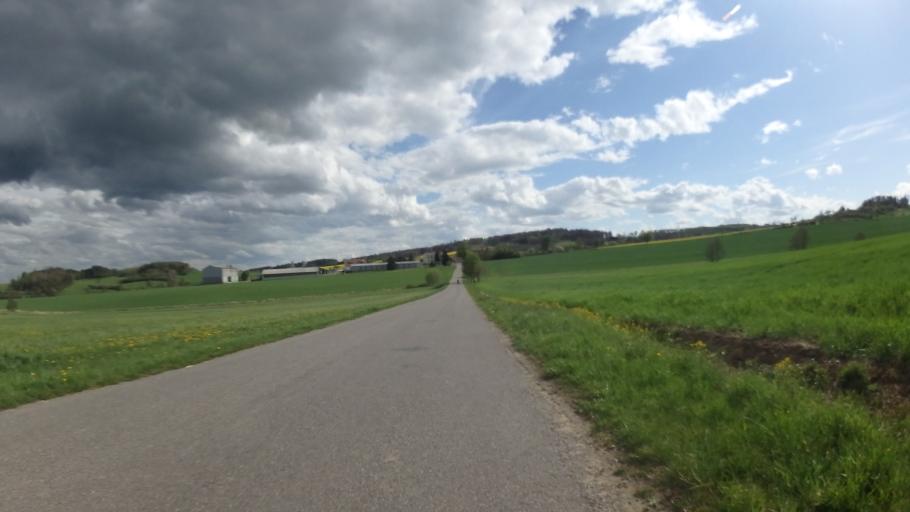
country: CZ
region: Vysocina
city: Merin
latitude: 49.3549
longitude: 15.8783
